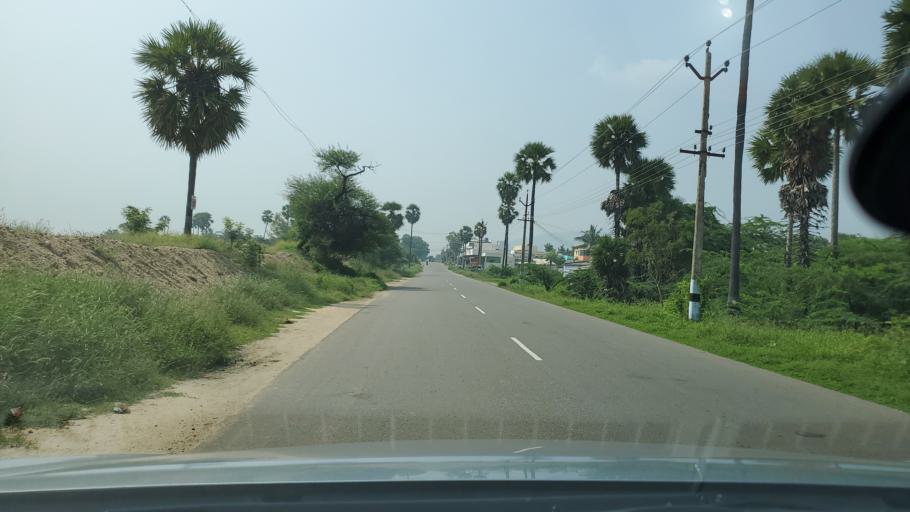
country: IN
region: Tamil Nadu
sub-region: Erode
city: Chennimalai
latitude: 11.1855
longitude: 77.6093
